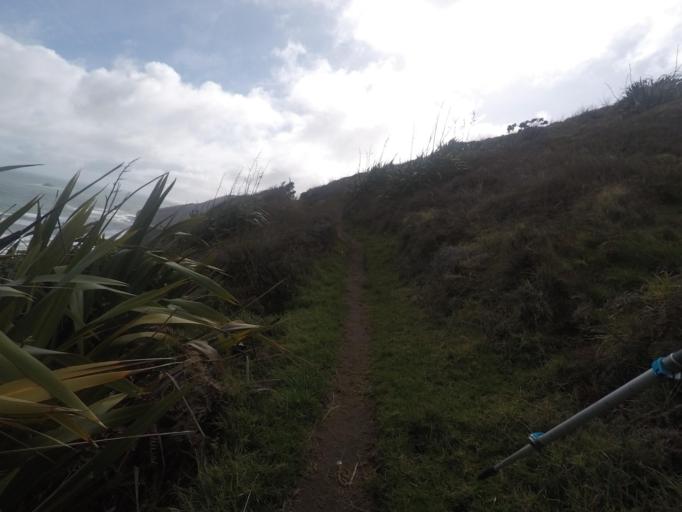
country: NZ
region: Auckland
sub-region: Auckland
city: Muriwai Beach
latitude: -36.8678
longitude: 174.4356
